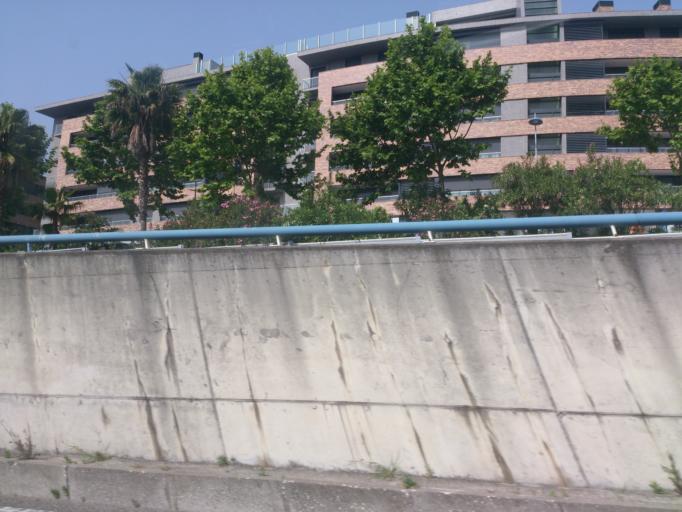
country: PT
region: Lisbon
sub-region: Loures
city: Moscavide
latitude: 38.7771
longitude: -9.1056
